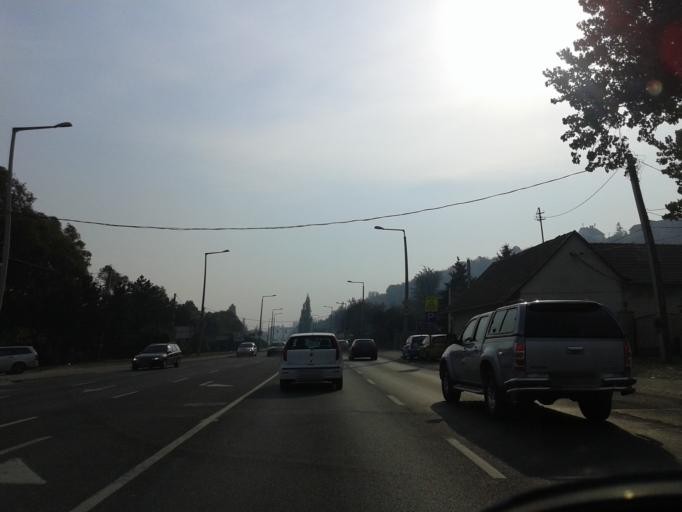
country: HU
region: Budapest
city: Budapest III. keruelet
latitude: 47.5591
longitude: 19.0250
